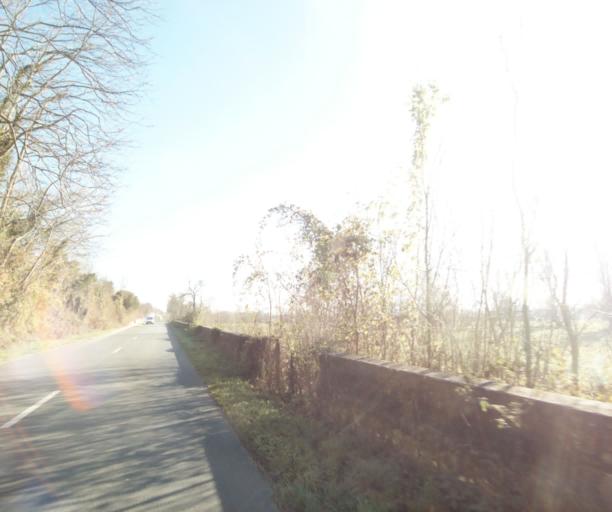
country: FR
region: Poitou-Charentes
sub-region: Departement de la Charente-Maritime
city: Les Gonds
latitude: 45.7310
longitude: -0.6006
